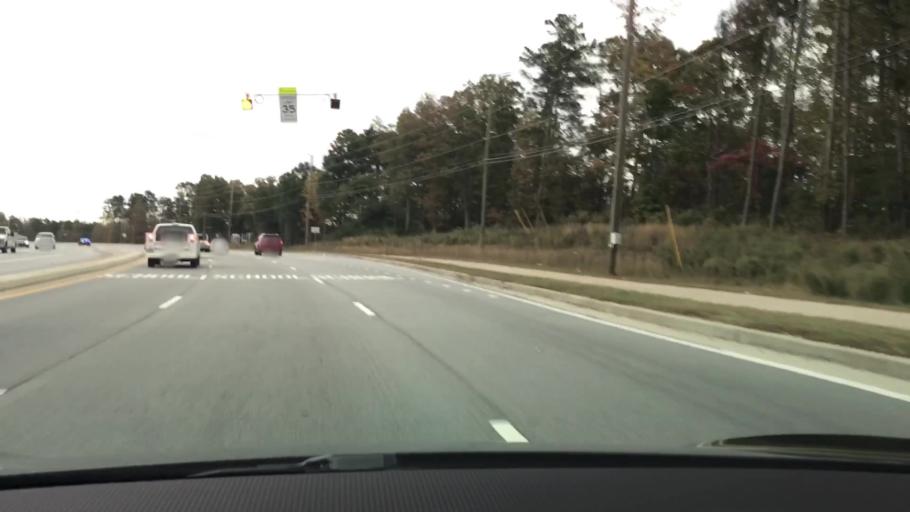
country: US
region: Georgia
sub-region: Hall County
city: Flowery Branch
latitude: 34.1352
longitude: -83.9445
